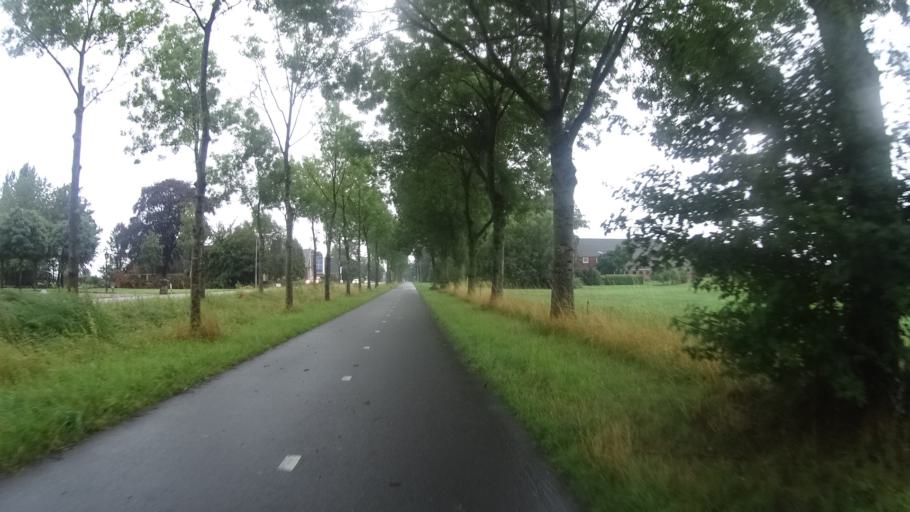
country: NL
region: Groningen
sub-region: Gemeente  Oldambt
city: Winschoten
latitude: 53.1599
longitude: 7.0797
